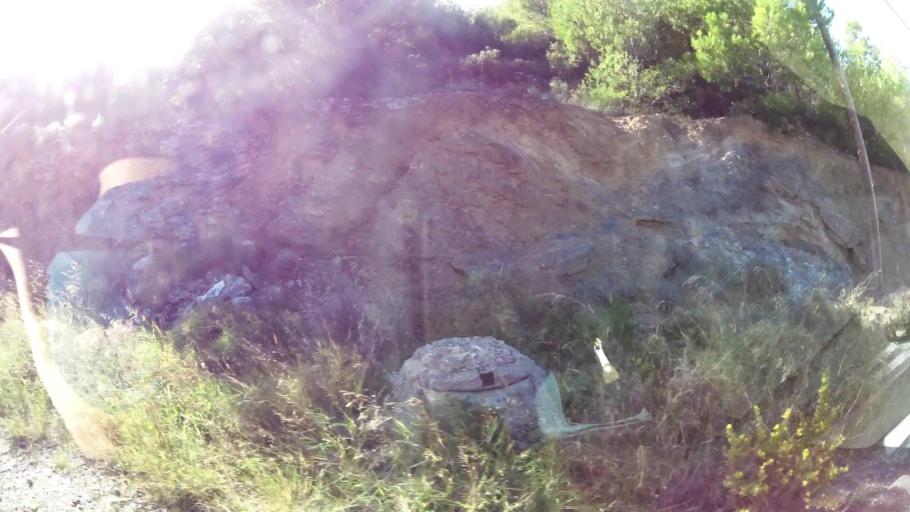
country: GR
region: Attica
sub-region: Nomarchia Anatolikis Attikis
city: Dioni
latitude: 38.0350
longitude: 23.9431
